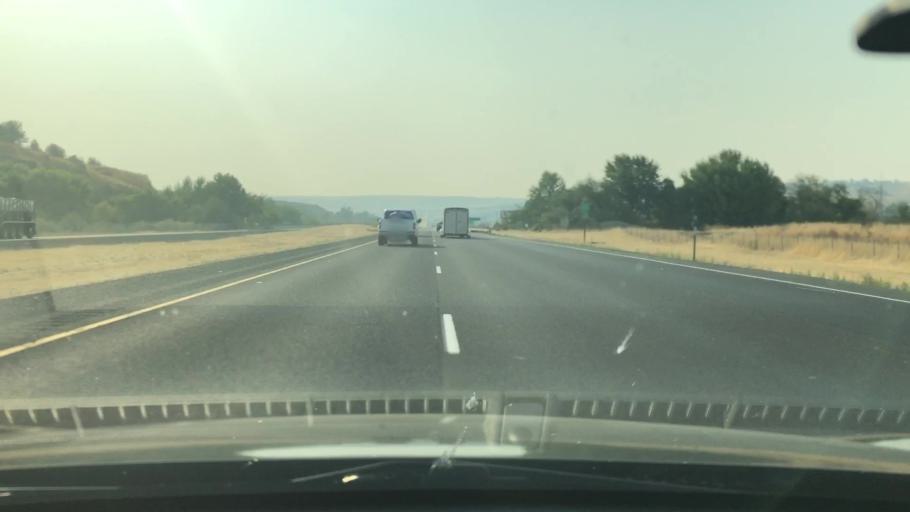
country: US
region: Oregon
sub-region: Umatilla County
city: Pendleton
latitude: 45.6657
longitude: -118.8137
